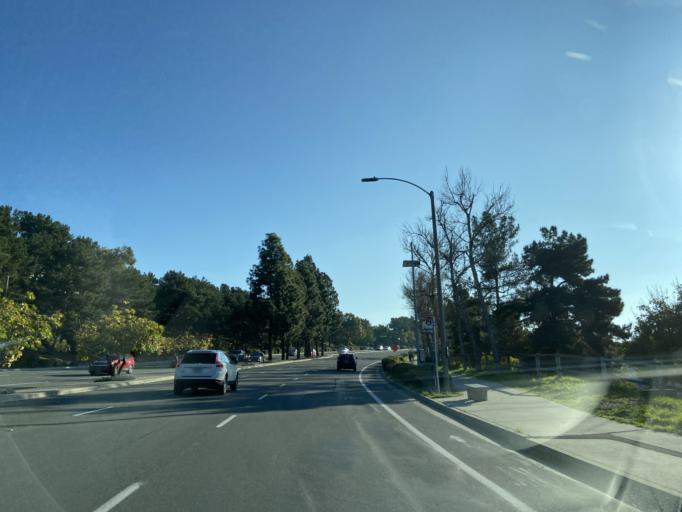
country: US
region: California
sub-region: San Diego County
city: Bonita
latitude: 32.6469
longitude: -116.9651
